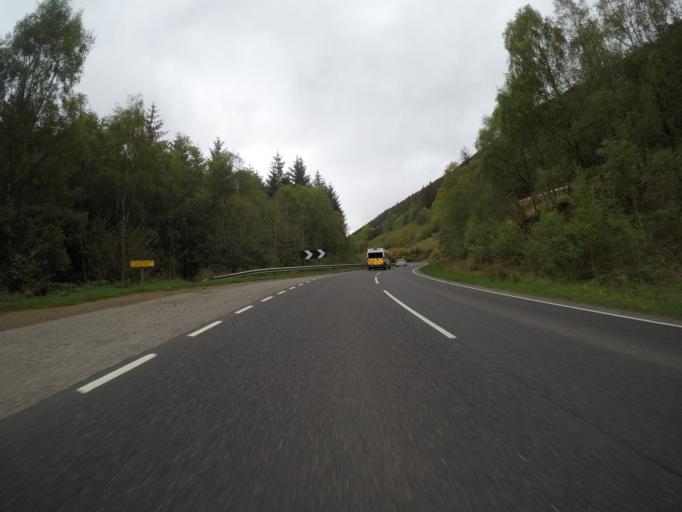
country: GB
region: Scotland
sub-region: Highland
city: Spean Bridge
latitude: 57.0176
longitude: -4.8282
